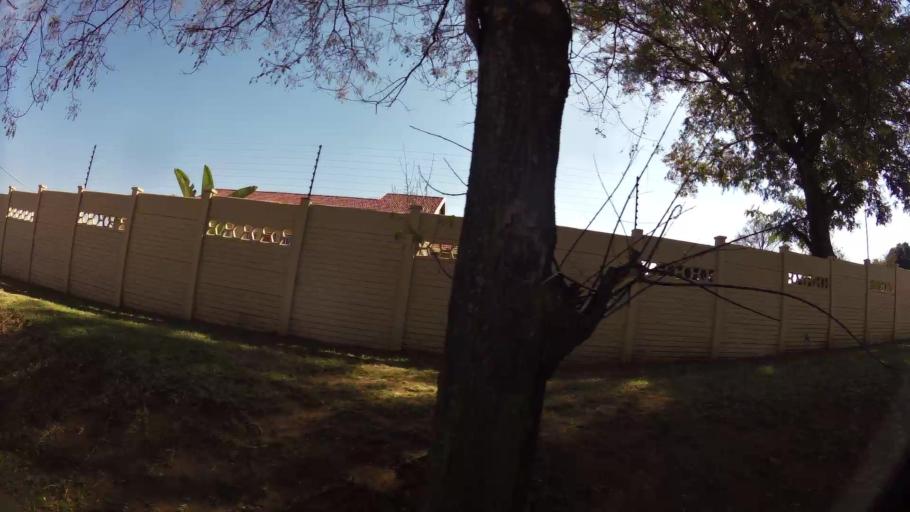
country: ZA
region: Gauteng
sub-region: City of Johannesburg Metropolitan Municipality
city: Johannesburg
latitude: -26.2754
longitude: 27.9907
